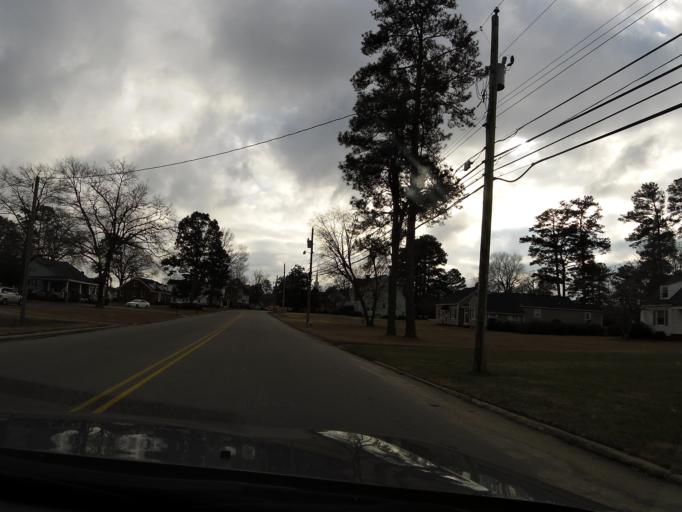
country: US
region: North Carolina
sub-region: Edgecombe County
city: Pinetops
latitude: 35.7941
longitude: -77.6377
